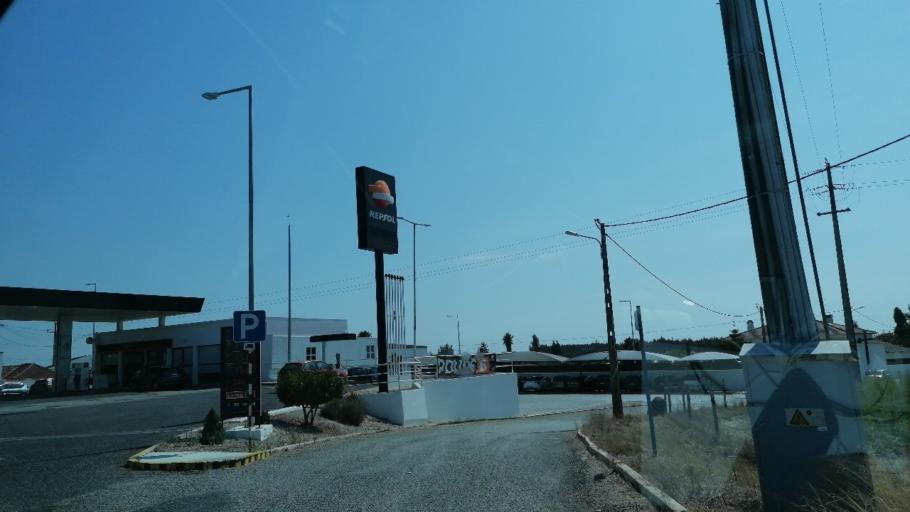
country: PT
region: Santarem
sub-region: Benavente
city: Poceirao
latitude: 38.7438
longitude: -8.6611
